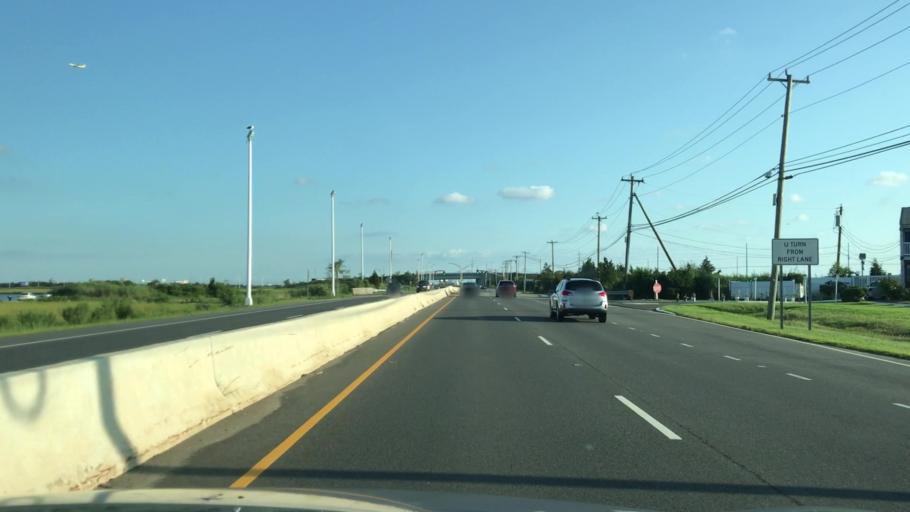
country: US
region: New Jersey
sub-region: Atlantic County
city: Absecon
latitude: 39.4009
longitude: -74.4923
